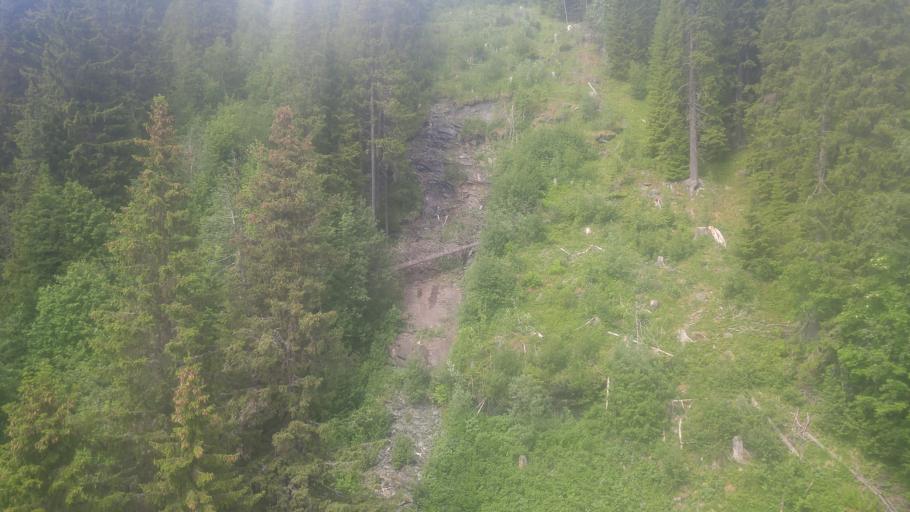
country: SE
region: Jaemtland
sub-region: Are Kommun
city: Are
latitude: 63.4051
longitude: 13.0766
